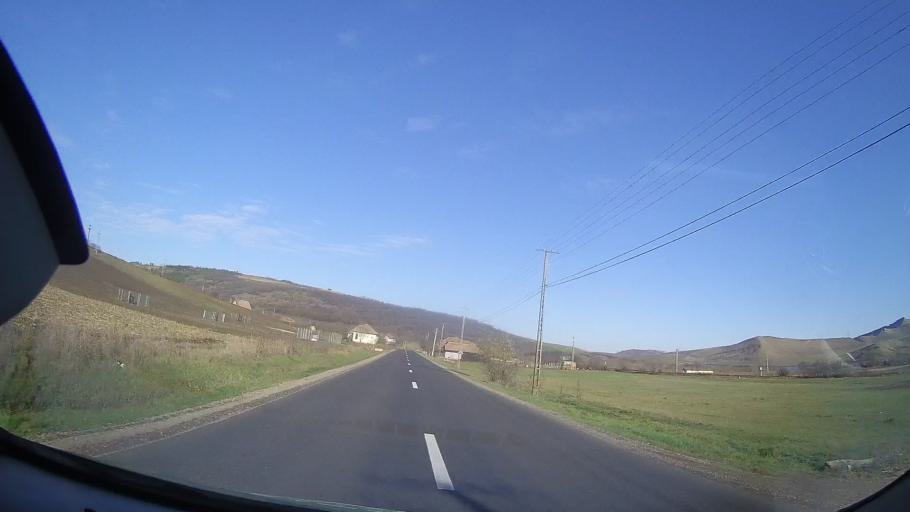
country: RO
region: Mures
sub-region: Comuna Zau De Campie
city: Zau de Campie
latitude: 46.6335
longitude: 24.1338
